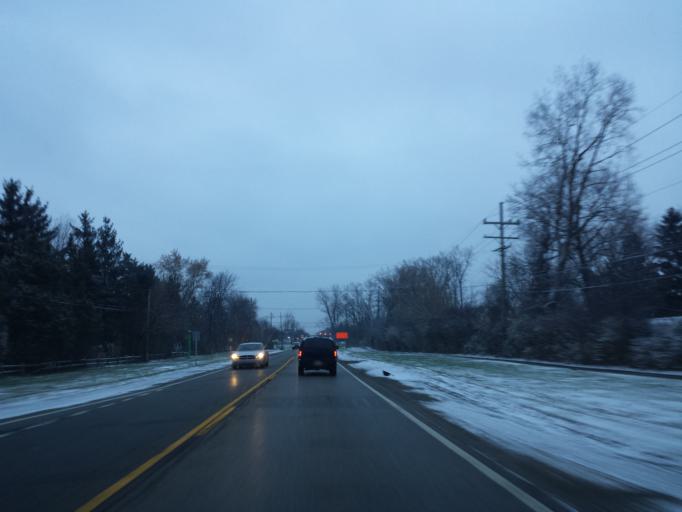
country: US
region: Michigan
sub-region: Oakland County
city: Franklin
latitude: 42.5328
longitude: -83.3407
